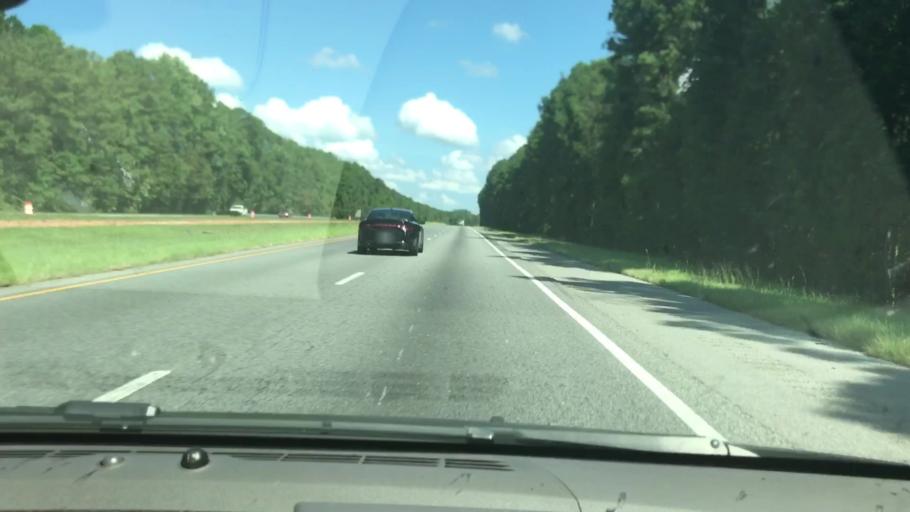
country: US
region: Georgia
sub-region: Harris County
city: Hamilton
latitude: 32.7620
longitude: -85.0173
